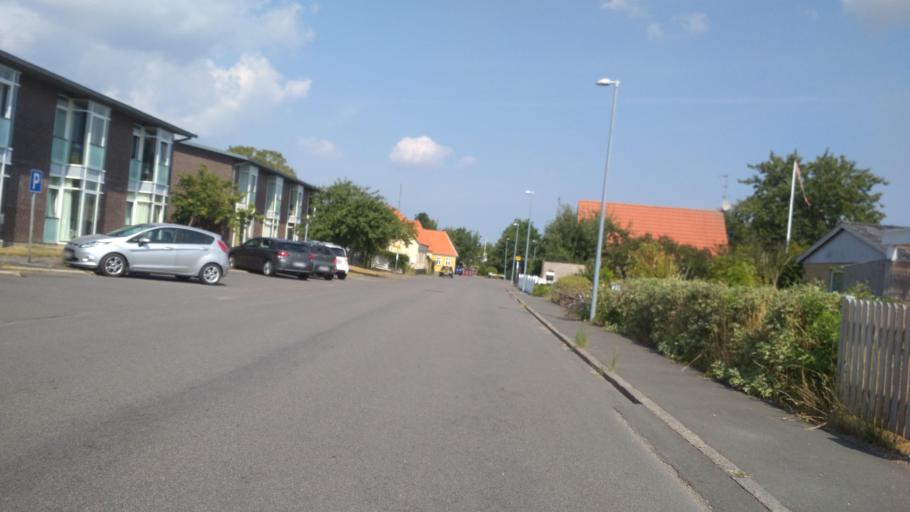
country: DK
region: Capital Region
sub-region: Bornholm Kommune
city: Akirkeby
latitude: 55.0698
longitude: 14.9272
